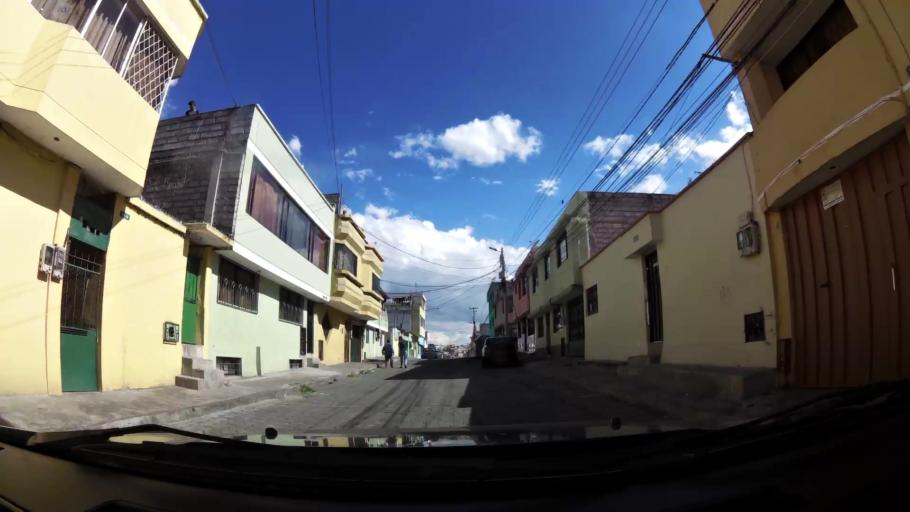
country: EC
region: Pichincha
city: Quito
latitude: -0.1214
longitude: -78.4645
